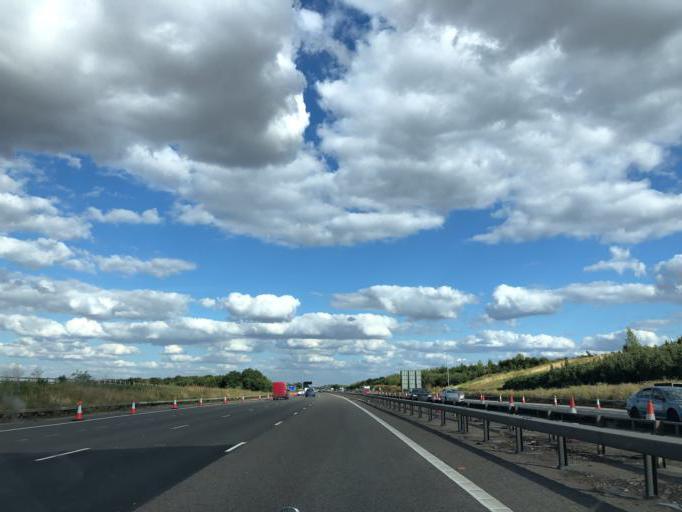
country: GB
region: England
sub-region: Milton Keynes
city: Broughton
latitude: 52.0570
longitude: -0.6957
